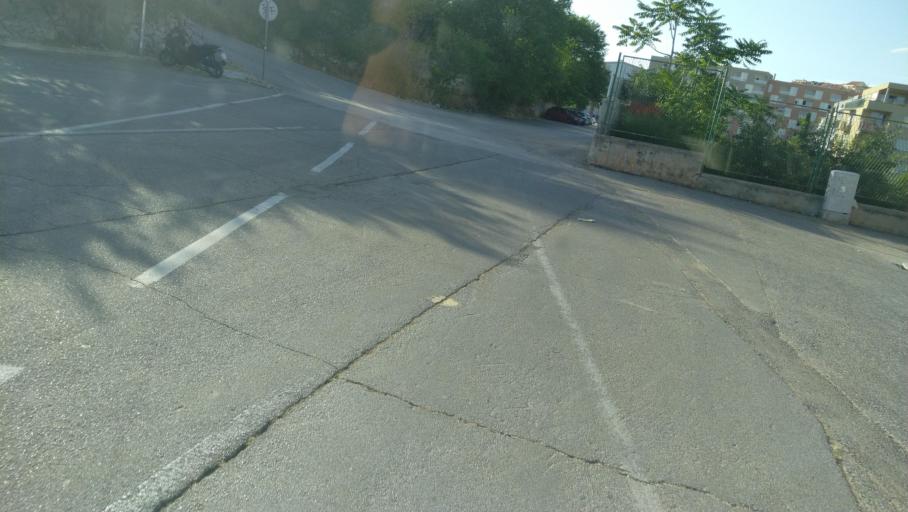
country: HR
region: Sibensko-Kniniska
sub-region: Grad Sibenik
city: Sibenik
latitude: 43.7436
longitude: 15.8953
